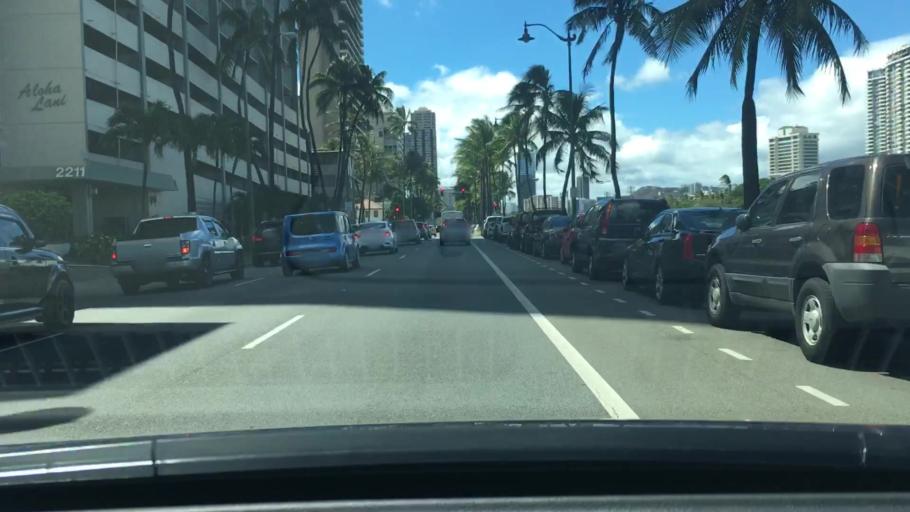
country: US
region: Hawaii
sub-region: Honolulu County
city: Honolulu
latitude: 21.2821
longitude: -157.8262
